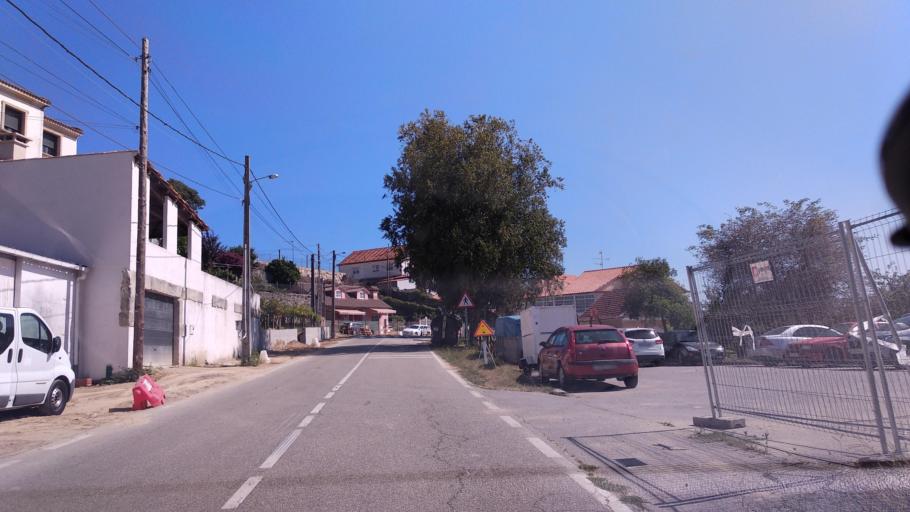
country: ES
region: Galicia
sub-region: Provincia de Pontevedra
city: Moana
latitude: 42.2824
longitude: -8.7505
